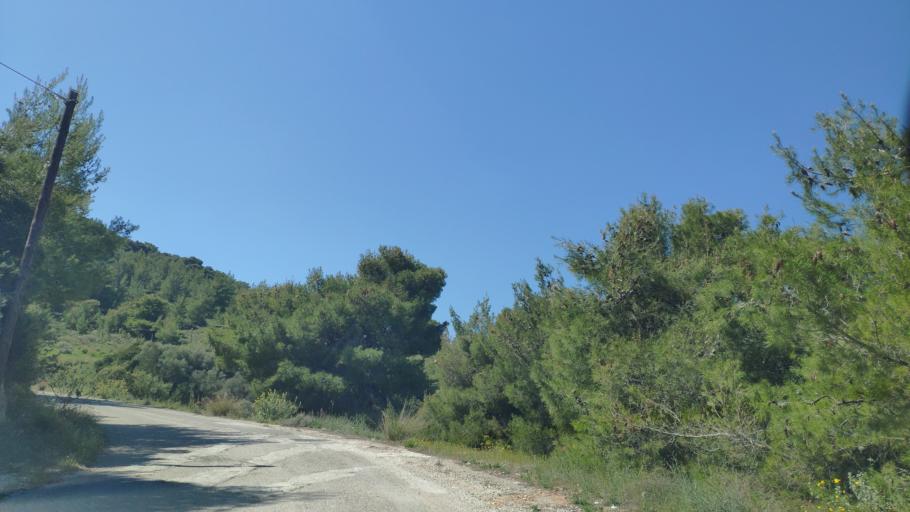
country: GR
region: Attica
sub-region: Nomarchia Athinas
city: Skaramangas
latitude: 38.0301
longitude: 23.6329
